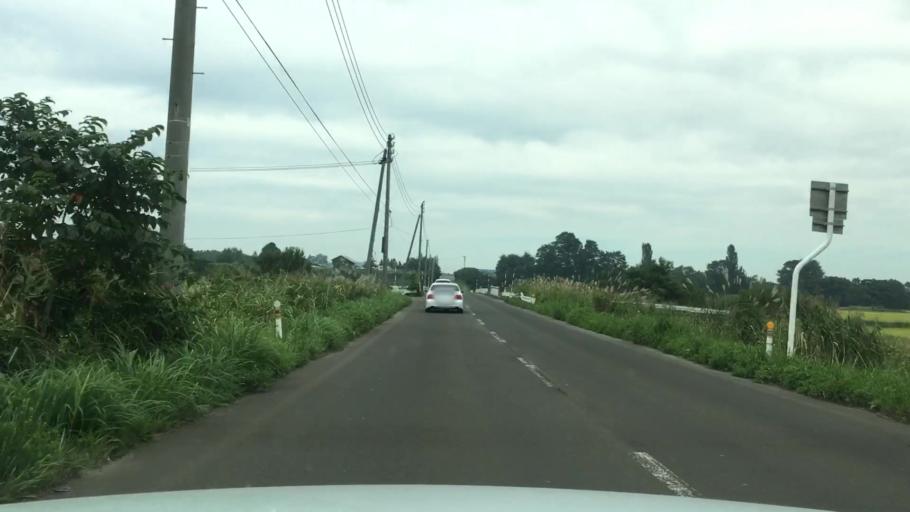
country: JP
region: Aomori
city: Hirosaki
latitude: 40.6497
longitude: 140.4226
